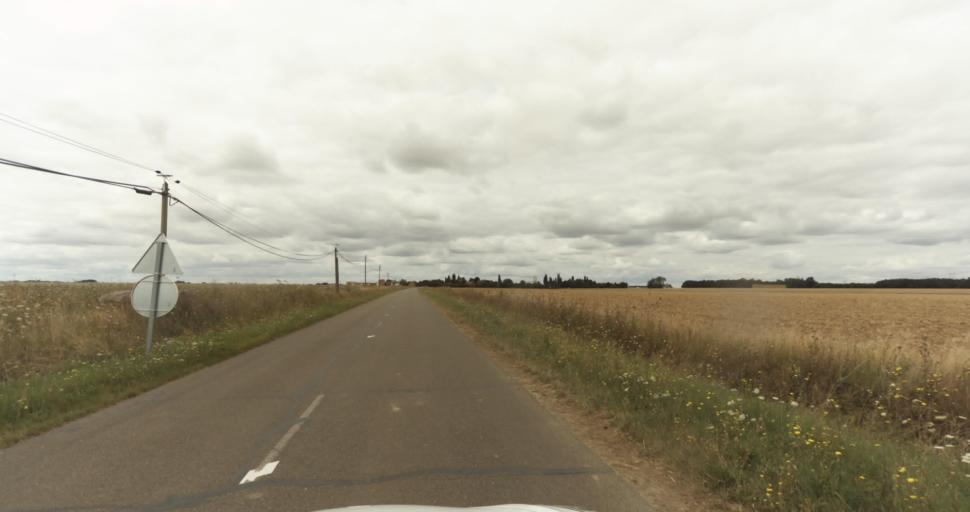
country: FR
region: Haute-Normandie
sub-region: Departement de l'Eure
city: La Madeleine-de-Nonancourt
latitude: 48.8326
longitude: 1.2110
